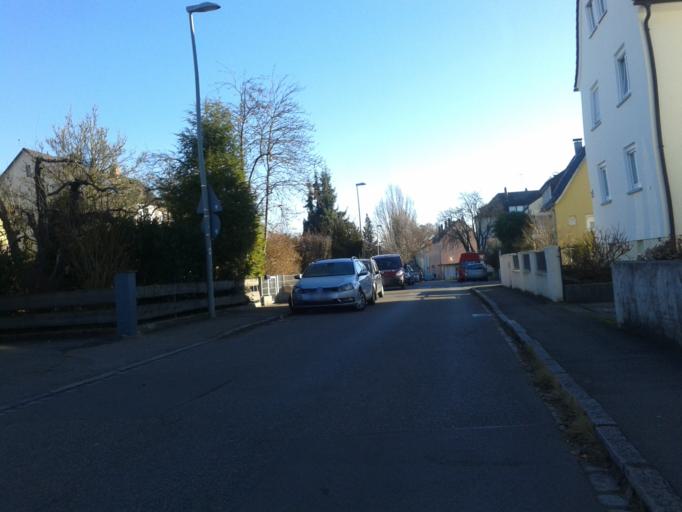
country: DE
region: Baden-Wuerttemberg
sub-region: Tuebingen Region
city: Ulm
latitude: 48.3899
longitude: 9.9649
